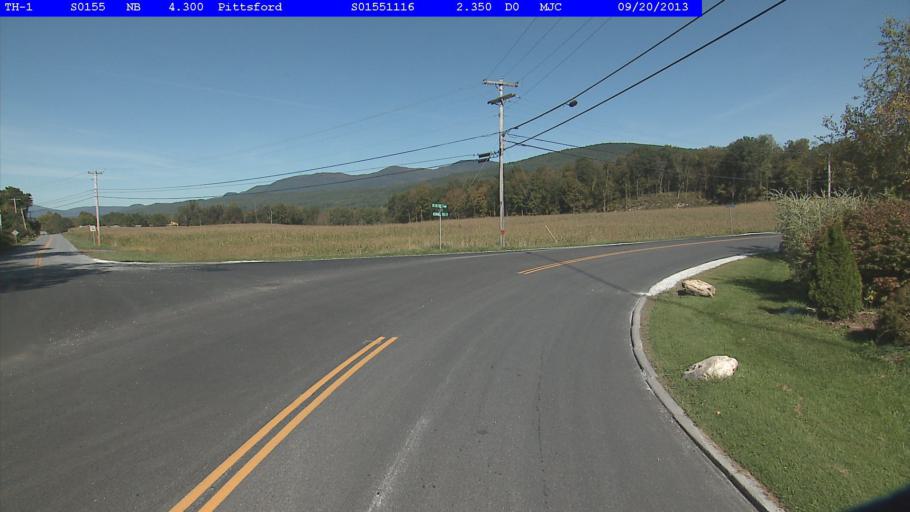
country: US
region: Vermont
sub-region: Rutland County
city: Brandon
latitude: 43.7213
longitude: -73.0588
